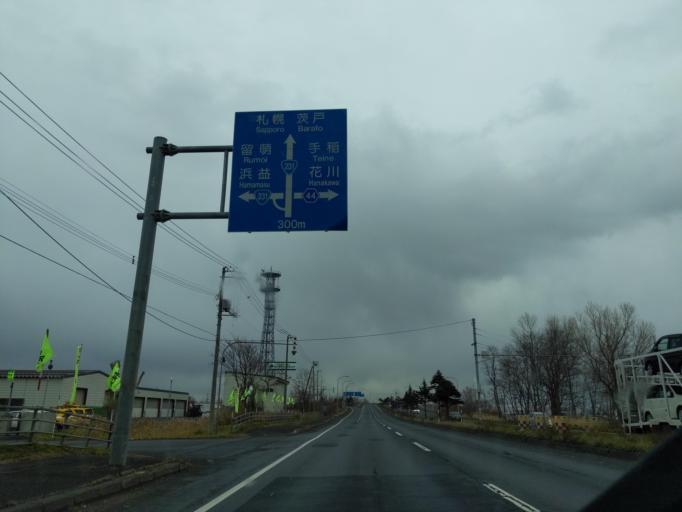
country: JP
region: Hokkaido
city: Ishikari
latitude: 43.1852
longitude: 141.3173
